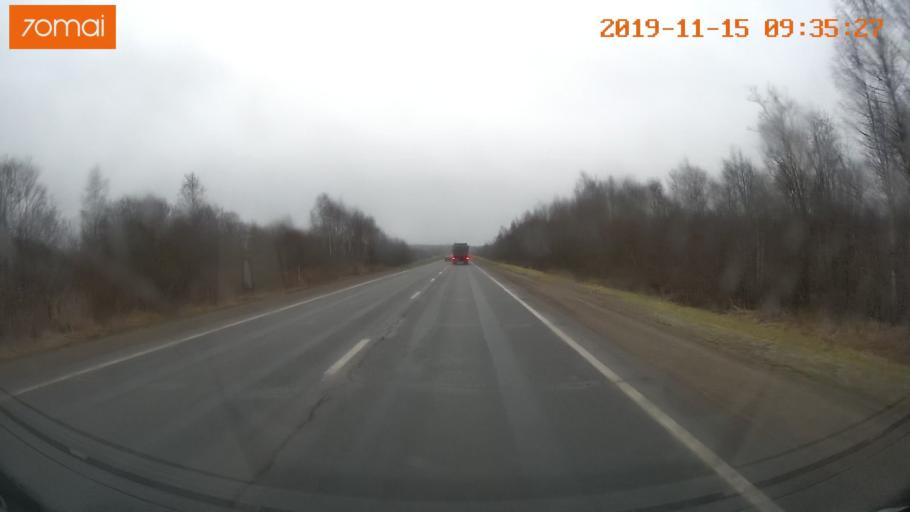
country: RU
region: Vologda
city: Sheksna
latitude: 59.2545
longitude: 38.3988
